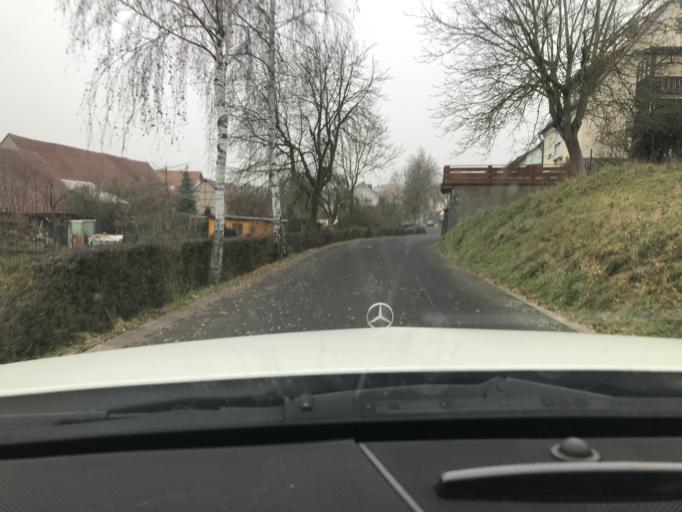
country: DE
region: Bavaria
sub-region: Regierungsbezirk Unterfranken
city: Werneck
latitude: 50.0002
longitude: 10.0680
